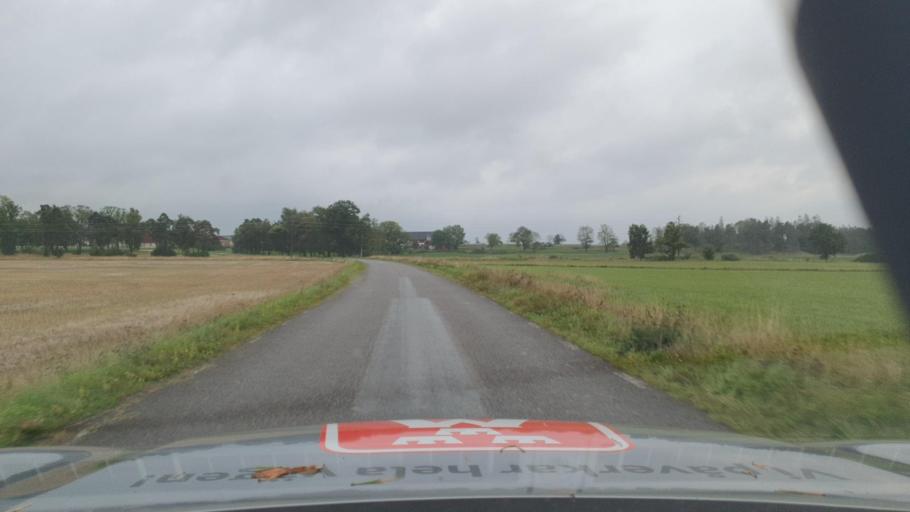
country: SE
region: Gotland
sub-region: Gotland
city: Visby
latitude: 57.4869
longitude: 18.4563
